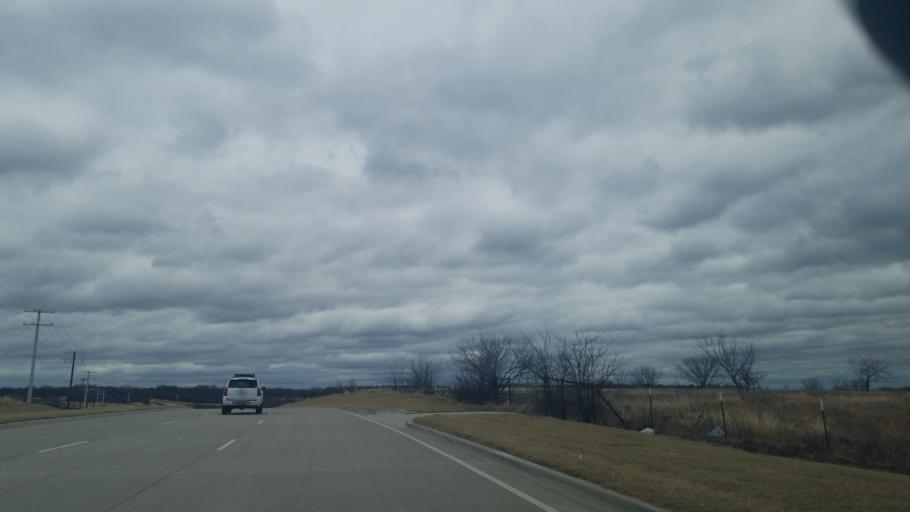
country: US
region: Texas
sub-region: Denton County
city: Trophy Club
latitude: 33.0510
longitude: -97.1887
